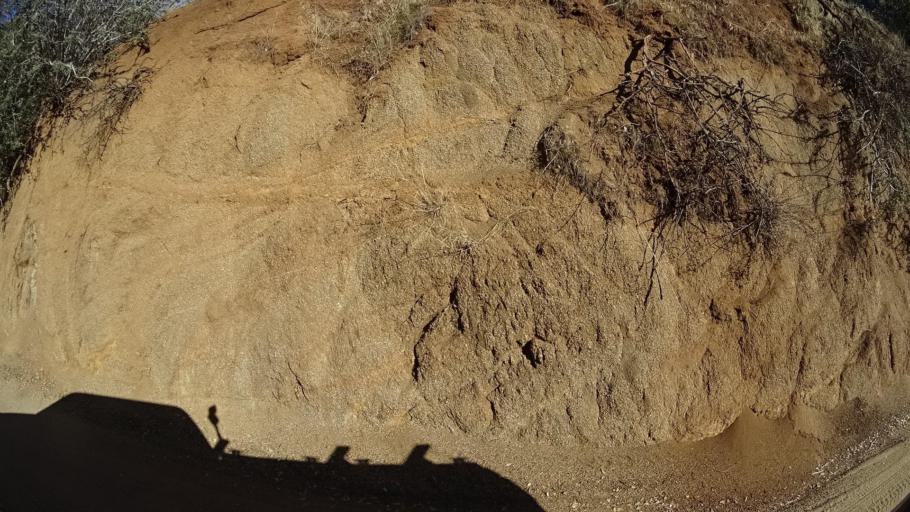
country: US
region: California
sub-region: Kern County
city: Bear Valley Springs
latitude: 35.3502
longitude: -118.5722
